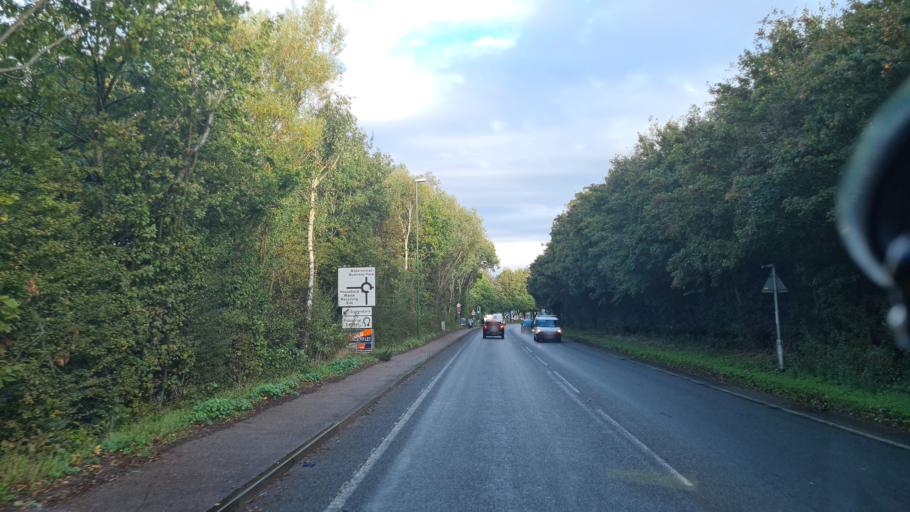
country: GB
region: England
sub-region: West Sussex
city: Littlehampton
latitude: 50.8217
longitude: -0.5471
